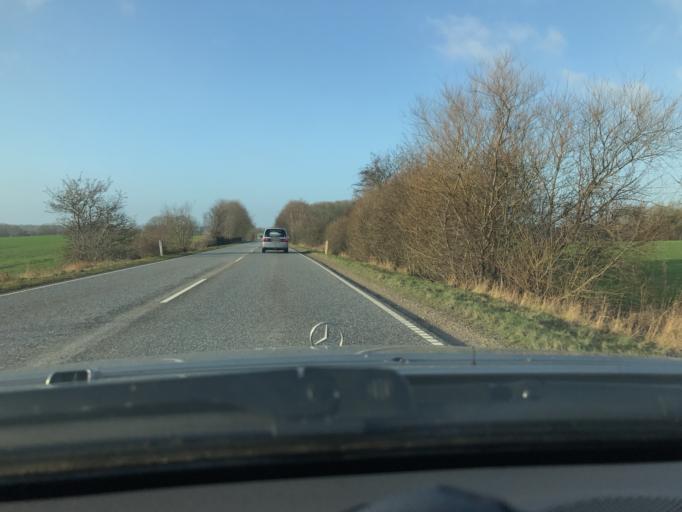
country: DK
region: South Denmark
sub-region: Sonderborg Kommune
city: Horuphav
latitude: 54.9216
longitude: 9.8912
